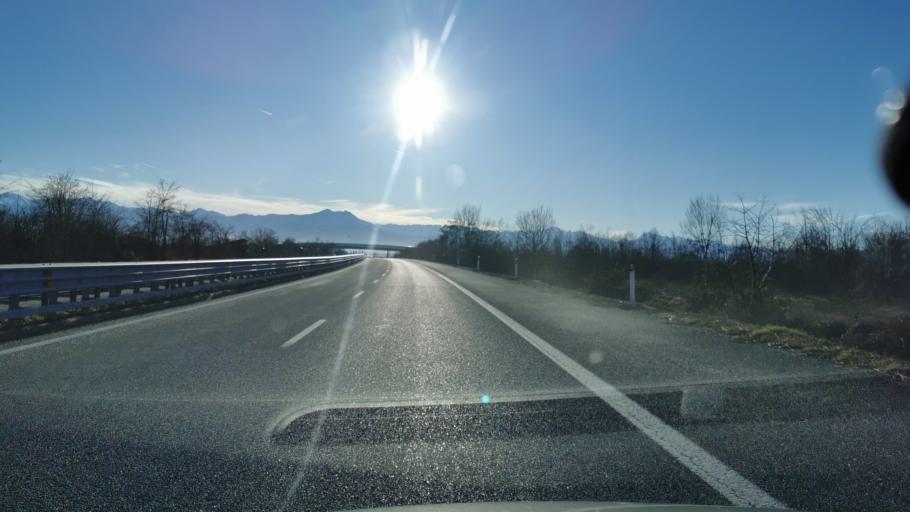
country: IT
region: Piedmont
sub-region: Provincia di Cuneo
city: Magliano Alpi
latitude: 44.4792
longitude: 7.7943
